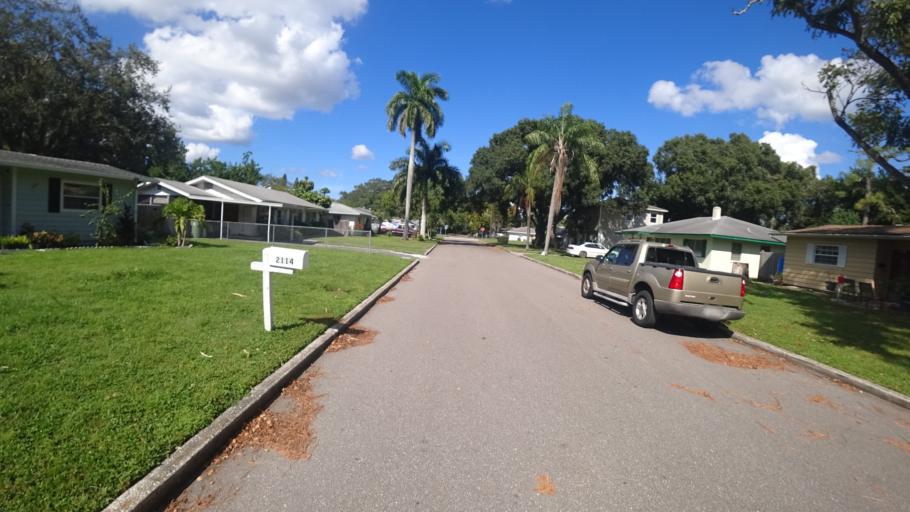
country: US
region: Florida
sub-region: Manatee County
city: South Bradenton
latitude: 27.4802
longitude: -82.5820
